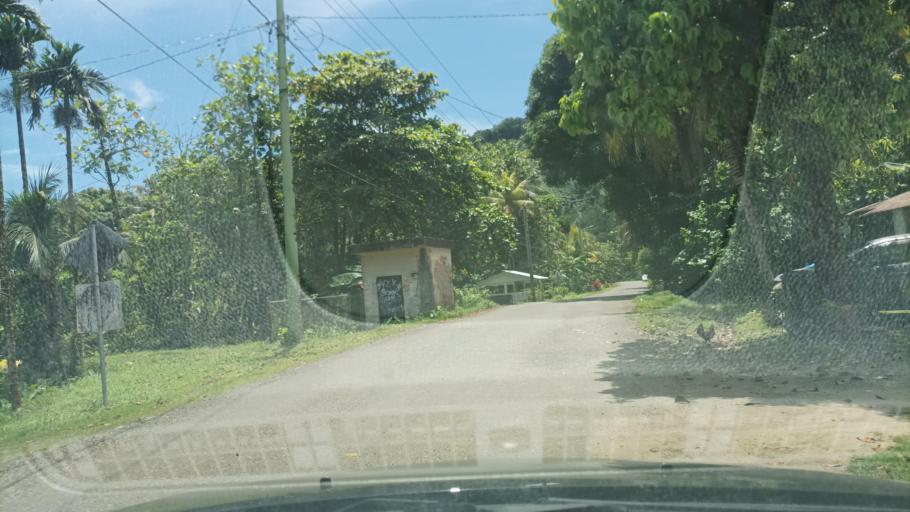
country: FM
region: Kosrae
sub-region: Tafunsak Municipality
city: Tafunsak
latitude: 5.3647
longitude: 162.9884
